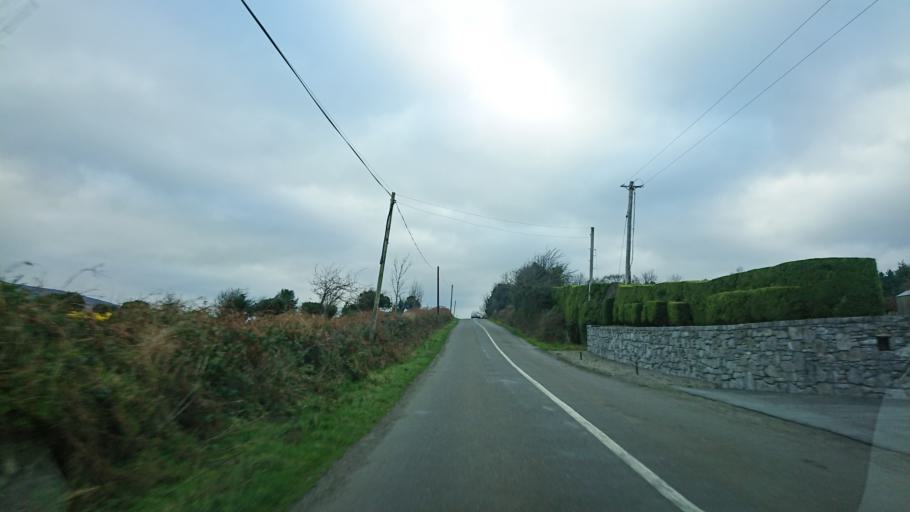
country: IE
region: Munster
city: Carrick-on-Suir
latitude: 52.3198
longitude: -7.5590
